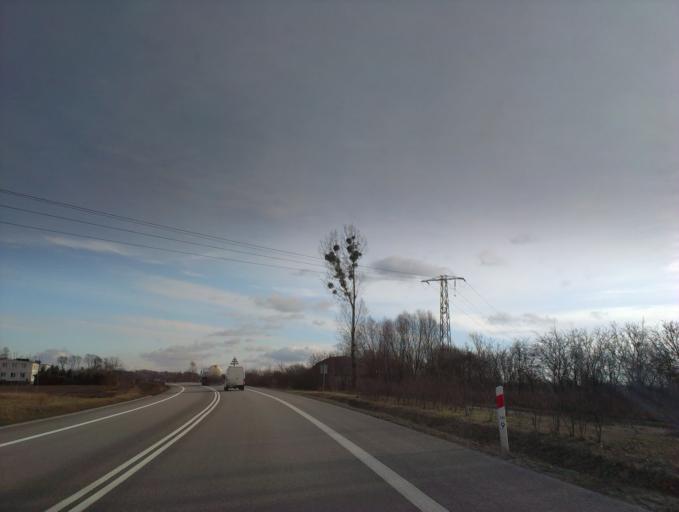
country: PL
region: Kujawsko-Pomorskie
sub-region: Powiat lipnowski
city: Kikol
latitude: 52.9189
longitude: 19.0989
